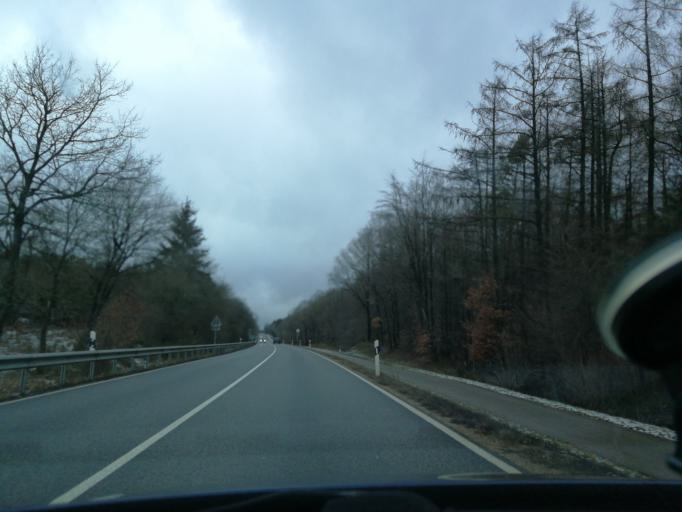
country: DE
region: Rheinland-Pfalz
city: Ohlenhard
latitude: 50.4311
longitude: 6.7410
